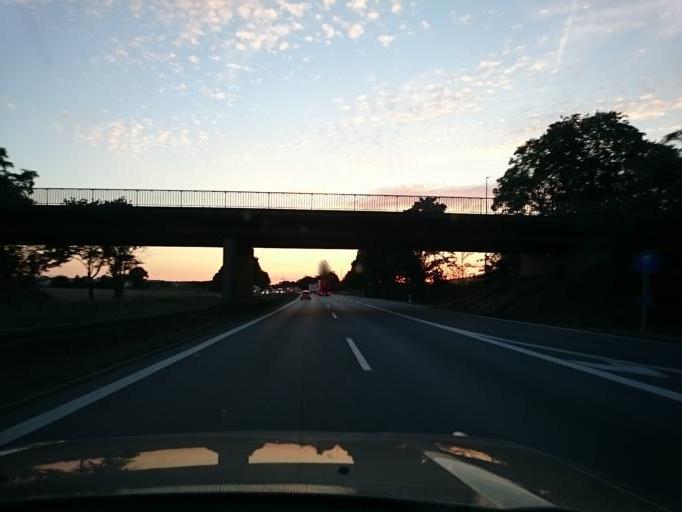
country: DE
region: Bavaria
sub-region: Upper Palatinate
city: Tegernheim
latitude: 49.0005
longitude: 12.1803
